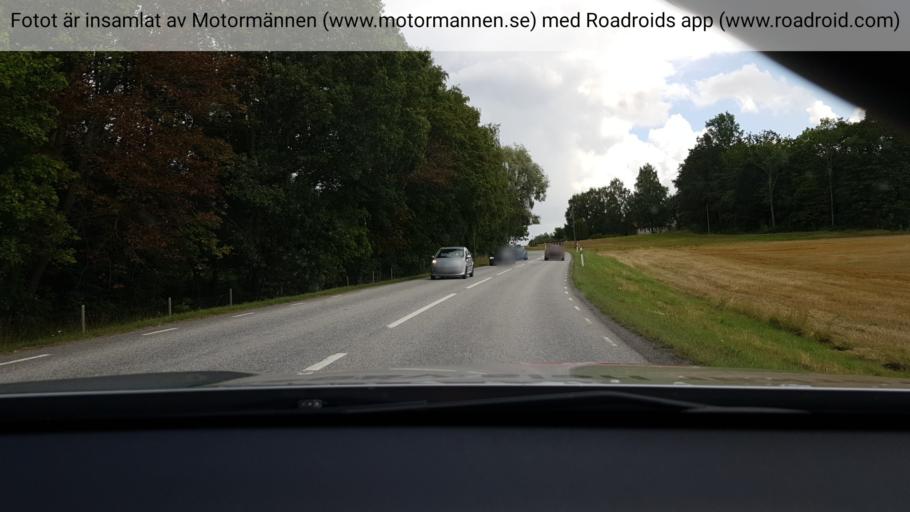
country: SE
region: Stockholm
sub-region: Salems Kommun
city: Ronninge
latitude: 59.2796
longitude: 17.7261
